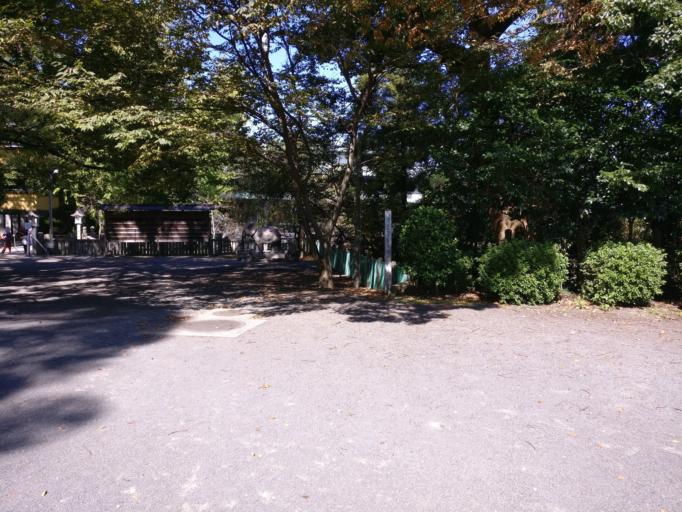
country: JP
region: Kagawa
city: Marugame
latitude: 34.1835
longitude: 133.8123
